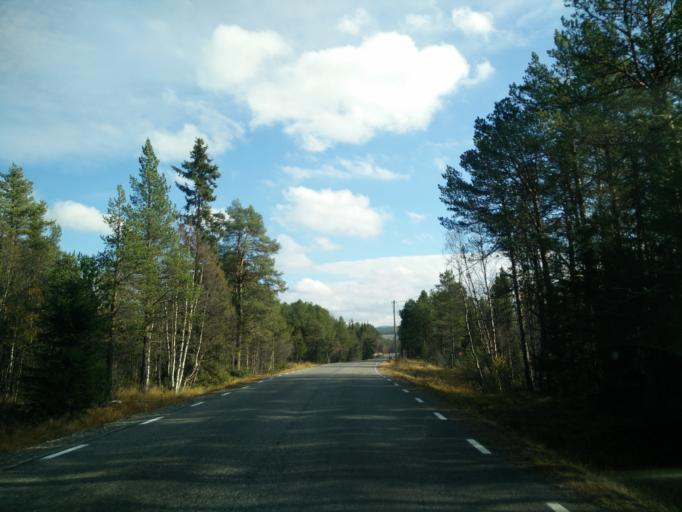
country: SE
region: Jaemtland
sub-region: Are Kommun
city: Are
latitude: 62.5499
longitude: 12.5899
